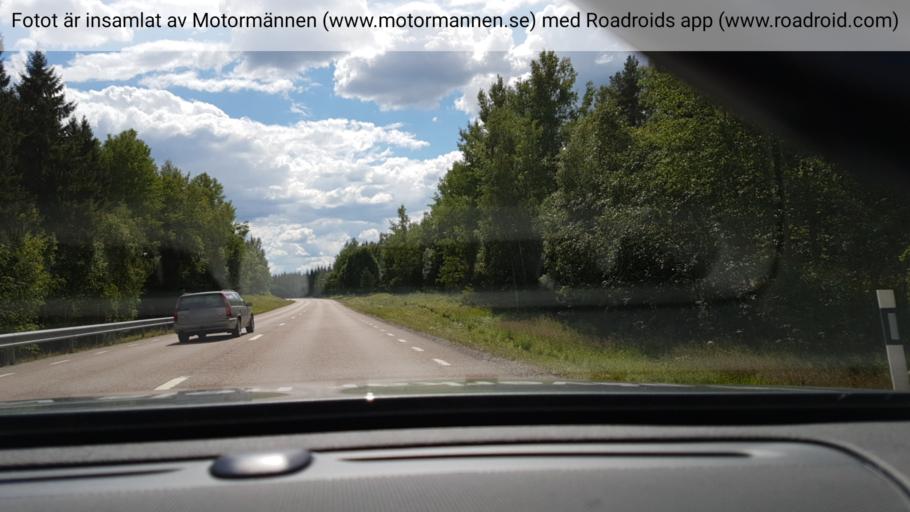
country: SE
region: Dalarna
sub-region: Faluns Kommun
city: Falun
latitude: 60.6564
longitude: 15.5538
